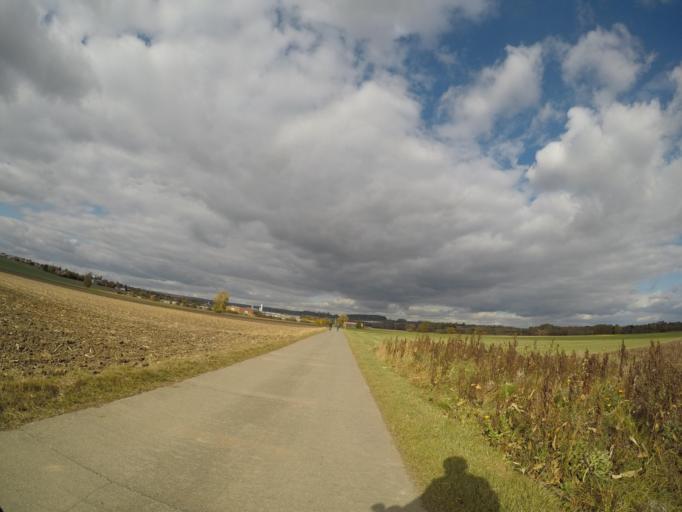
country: DE
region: Baden-Wuerttemberg
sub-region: Tuebingen Region
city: Emerkingen
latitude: 48.2207
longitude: 9.6569
